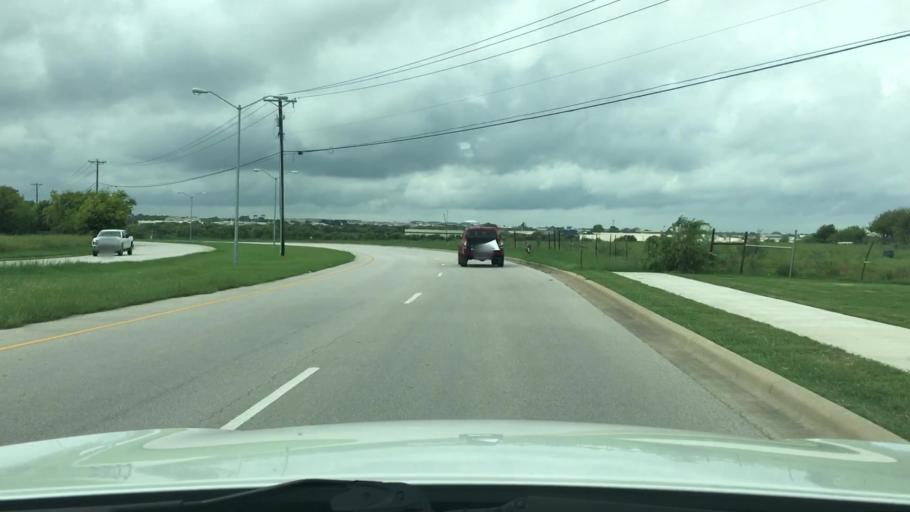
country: US
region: Texas
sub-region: Travis County
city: Windemere
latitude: 30.4795
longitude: -97.6659
